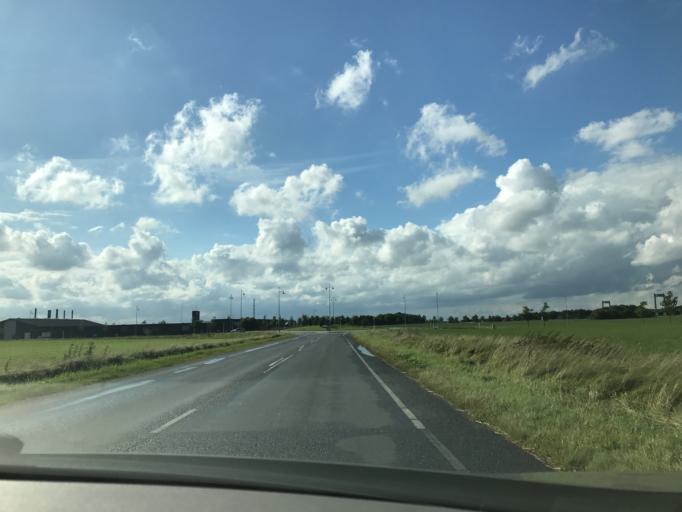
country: DK
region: South Denmark
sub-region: Middelfart Kommune
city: Strib
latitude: 55.5047
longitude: 9.7816
